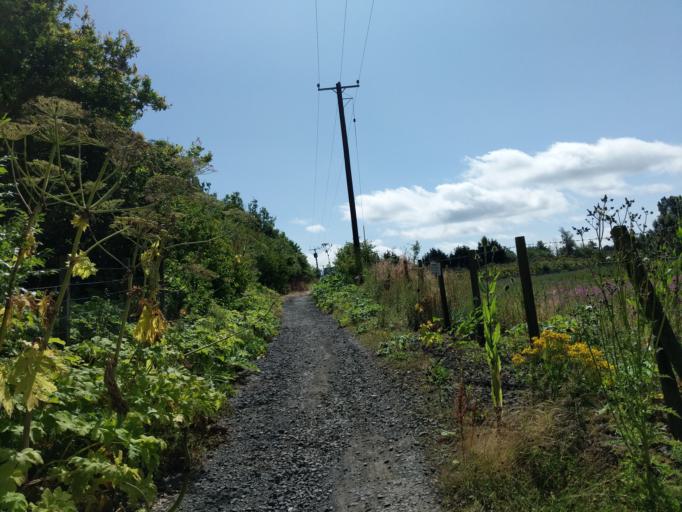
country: GB
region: Scotland
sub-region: Edinburgh
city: Currie
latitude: 55.9278
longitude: -3.3174
